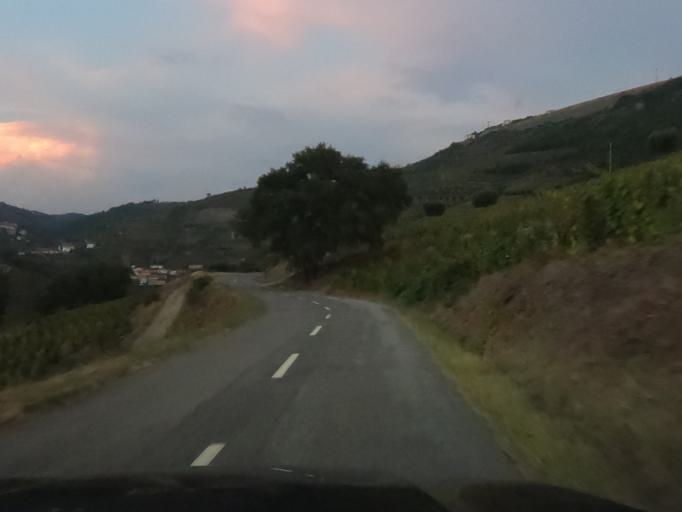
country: PT
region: Vila Real
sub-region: Santa Marta de Penaguiao
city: Santa Marta de Penaguiao
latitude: 41.2272
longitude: -7.7450
